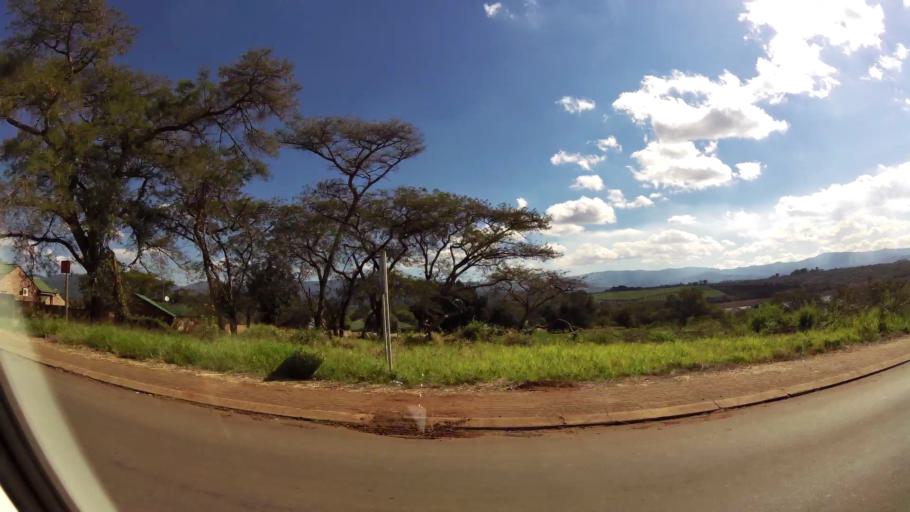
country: ZA
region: Limpopo
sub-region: Mopani District Municipality
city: Tzaneen
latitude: -23.8194
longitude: 30.1443
